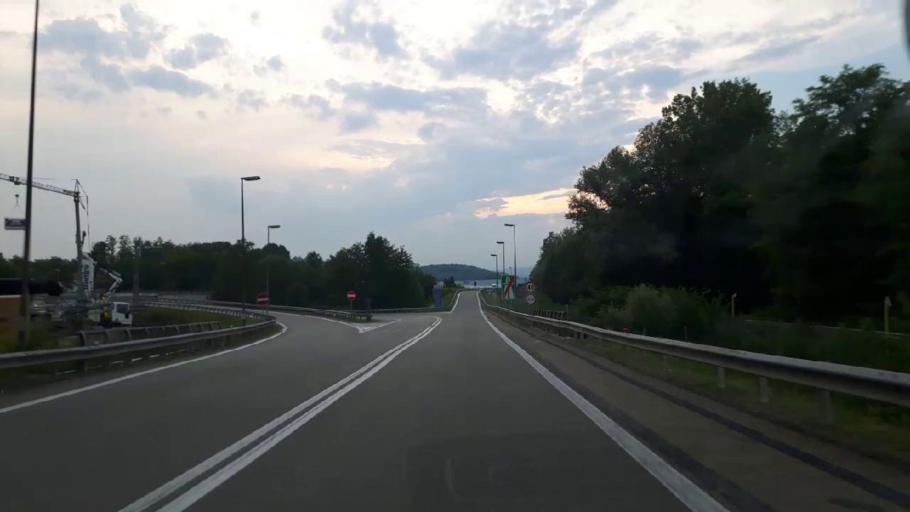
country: IT
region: Lombardy
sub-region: Provincia di Varese
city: Lisanza
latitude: 45.7146
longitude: 8.5946
